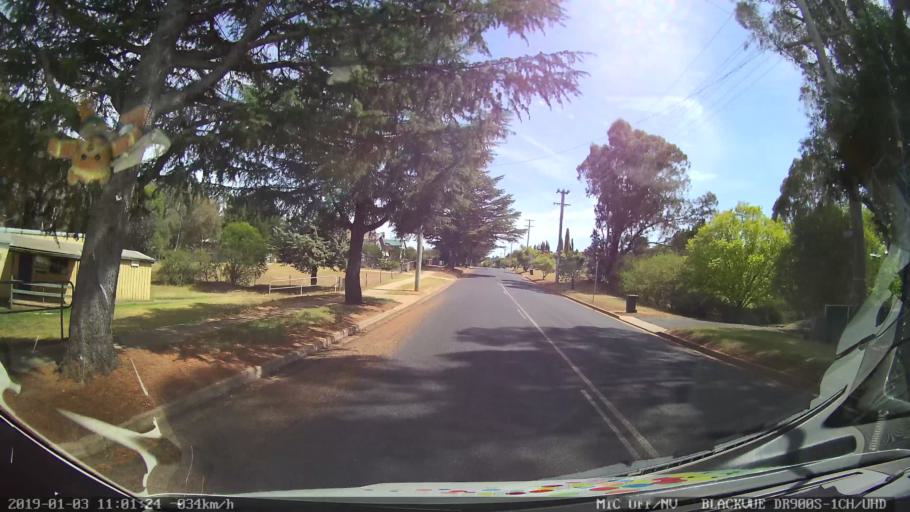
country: AU
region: New South Wales
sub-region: Young
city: Young
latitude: -34.3055
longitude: 148.2994
